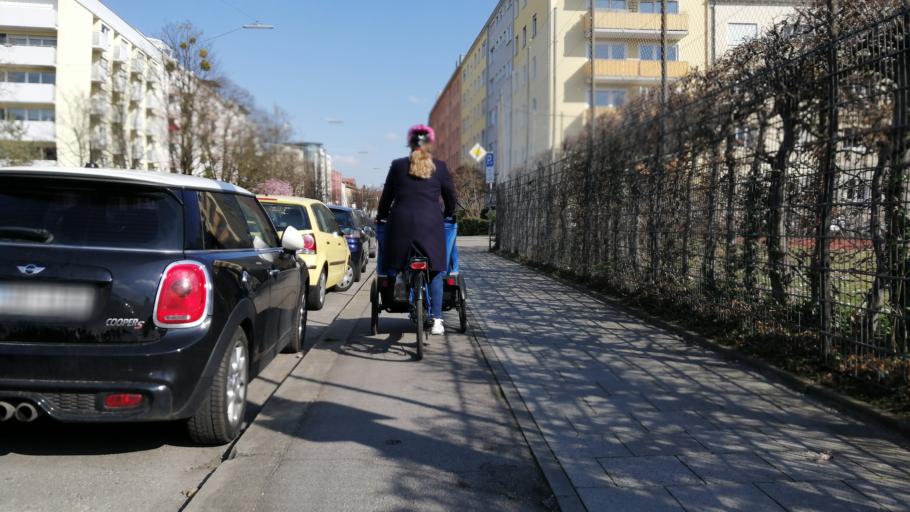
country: DE
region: Bavaria
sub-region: Upper Bavaria
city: Munich
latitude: 48.1671
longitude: 11.5837
